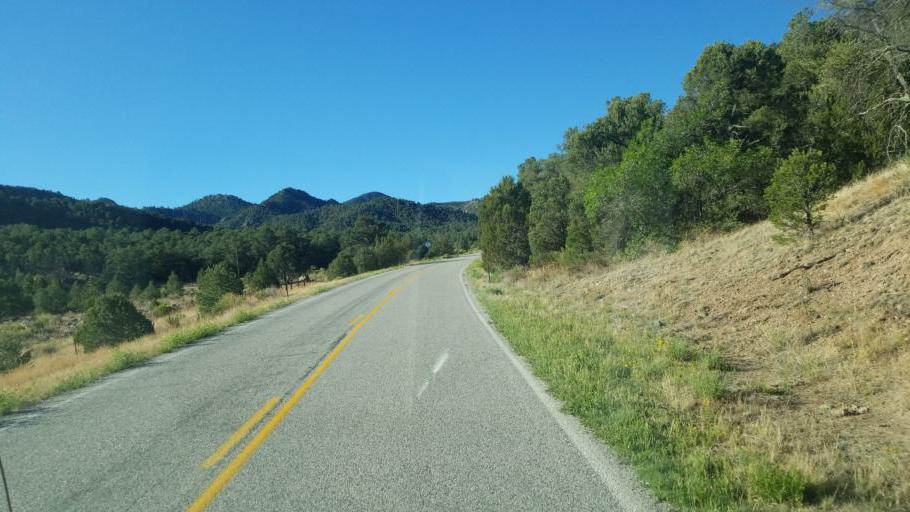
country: US
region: Colorado
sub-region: Custer County
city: Westcliffe
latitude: 38.3946
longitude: -105.5801
